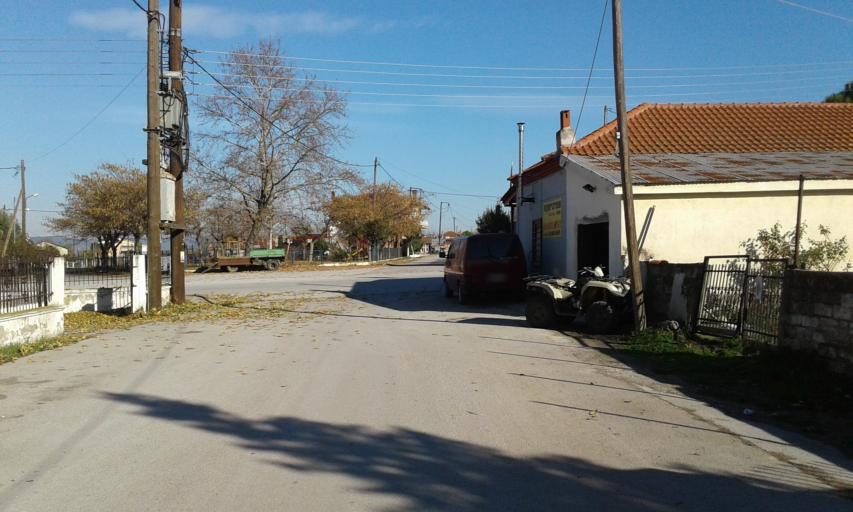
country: GR
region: Central Macedonia
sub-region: Nomos Thessalonikis
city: Gerakarou
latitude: 40.6368
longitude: 23.2462
